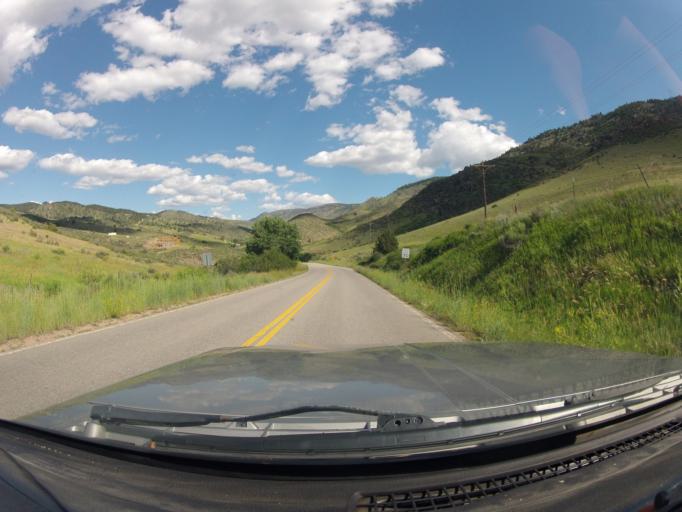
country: US
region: Colorado
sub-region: Larimer County
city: Laporte
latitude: 40.5340
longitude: -105.2713
